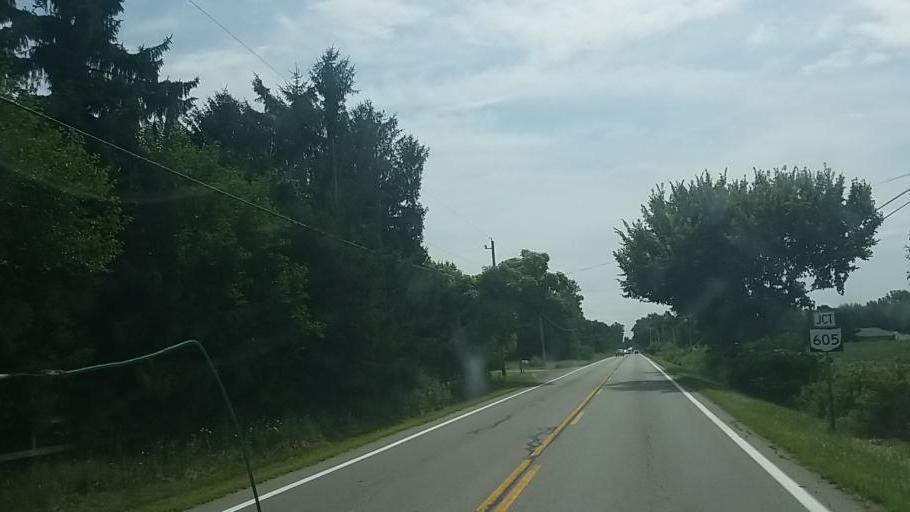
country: US
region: Ohio
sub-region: Delaware County
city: Sunbury
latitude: 40.2200
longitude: -82.8076
